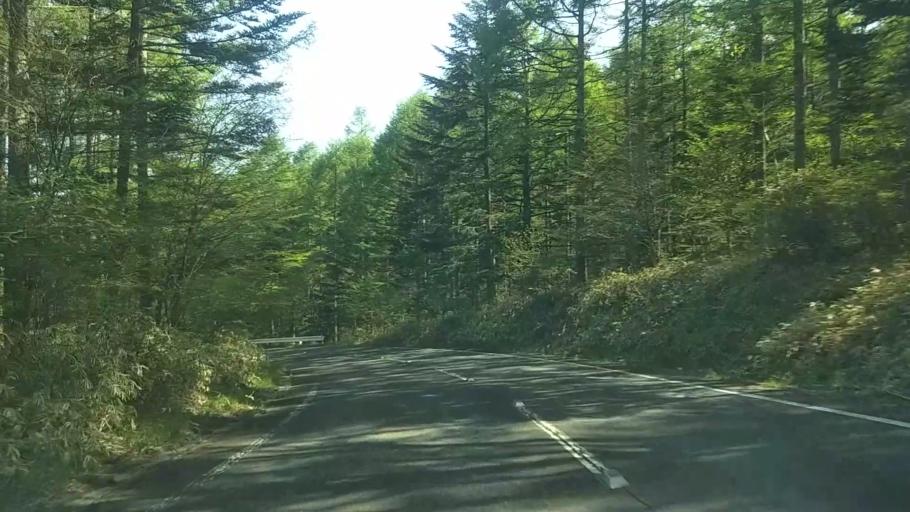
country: JP
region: Yamanashi
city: Nirasaki
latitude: 35.9232
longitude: 138.4011
